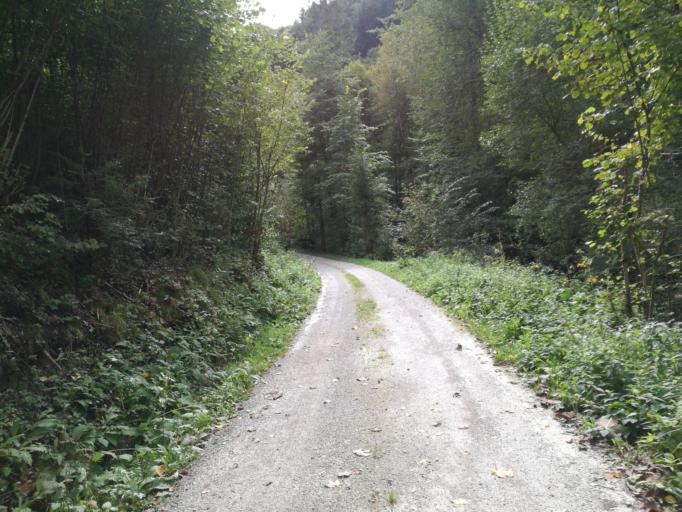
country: AT
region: Tyrol
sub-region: Politischer Bezirk Kufstein
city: Bad Haering
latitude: 47.5246
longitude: 12.1107
